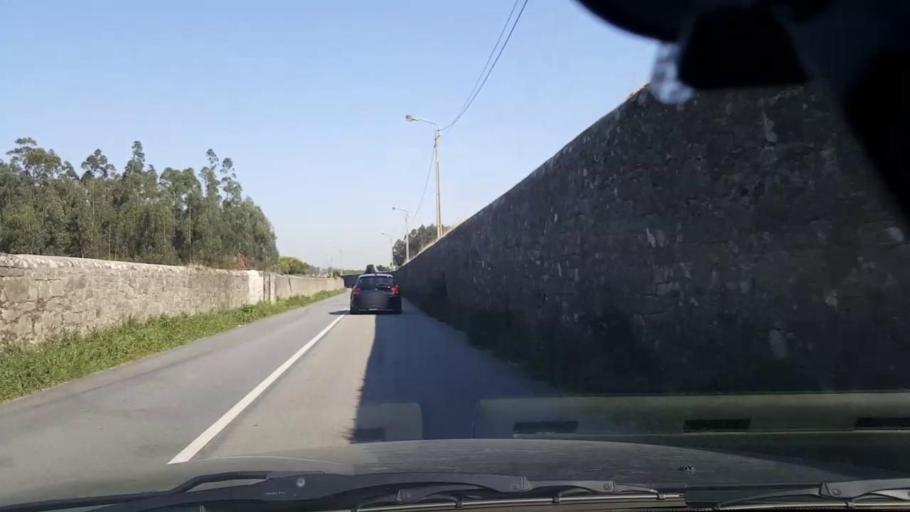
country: PT
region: Porto
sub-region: Vila do Conde
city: Arvore
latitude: 41.3297
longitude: -8.6802
